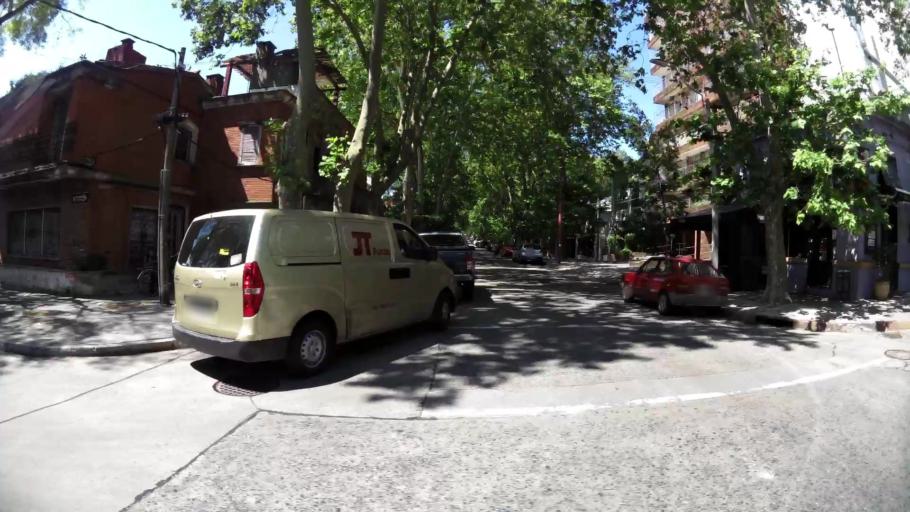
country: UY
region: Montevideo
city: Montevideo
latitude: -34.9195
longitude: -56.1600
